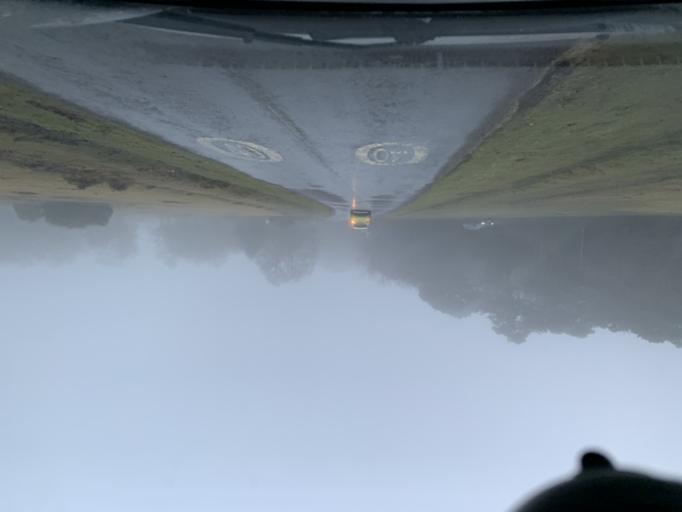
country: GB
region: England
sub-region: Hampshire
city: Cadnam
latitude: 50.9319
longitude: -1.6545
